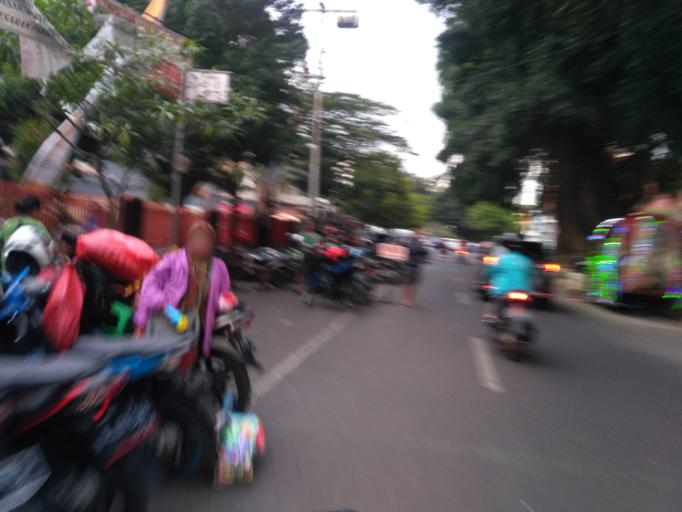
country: ID
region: East Java
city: Malang
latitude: -7.9834
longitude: 112.6306
